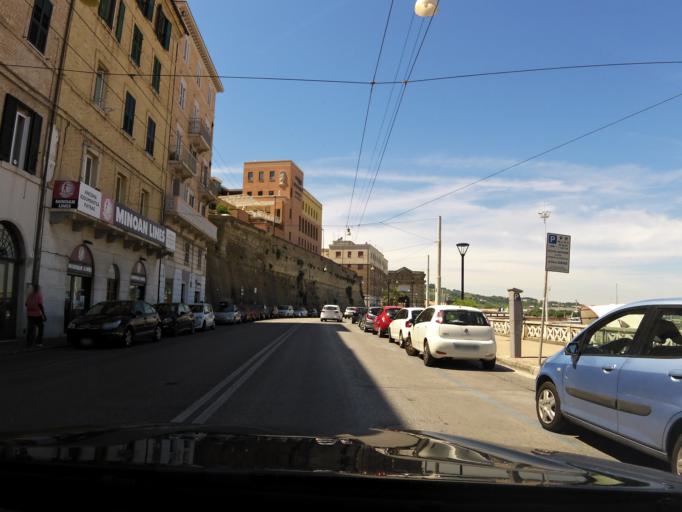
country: IT
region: The Marches
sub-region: Provincia di Ancona
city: Le Grazie di Ancona
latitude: 43.6169
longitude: 13.5073
